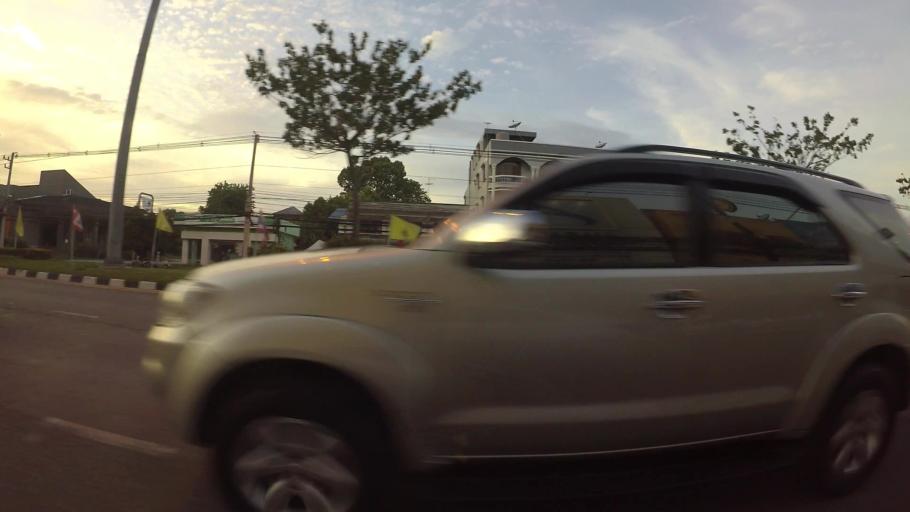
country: TH
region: Rayong
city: Rayong
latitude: 12.6823
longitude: 101.2642
